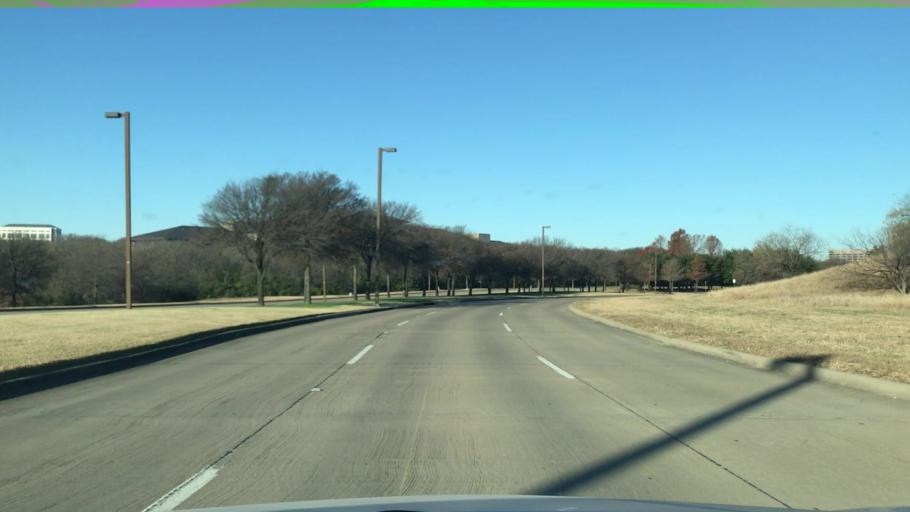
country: US
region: Texas
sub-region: Dallas County
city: Farmers Branch
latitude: 32.8898
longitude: -96.9454
